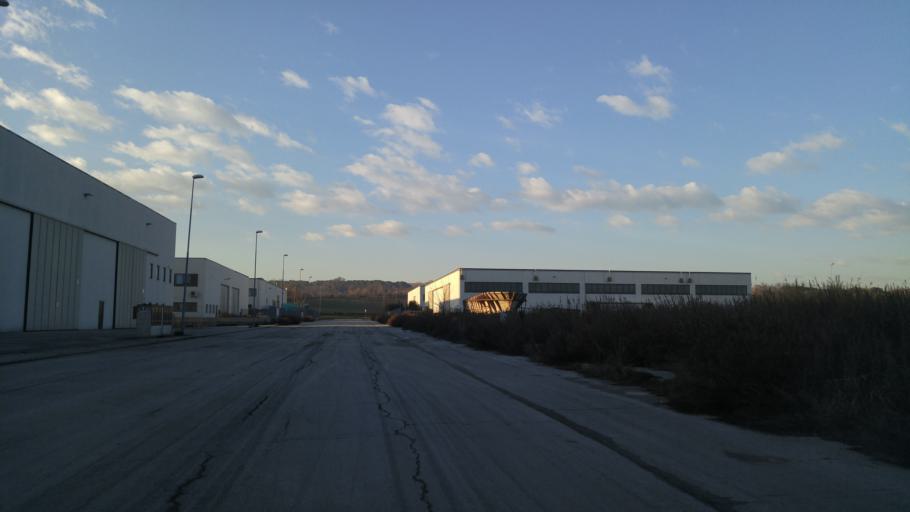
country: IT
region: The Marches
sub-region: Provincia di Ancona
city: Monterado
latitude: 43.7112
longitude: 13.0802
